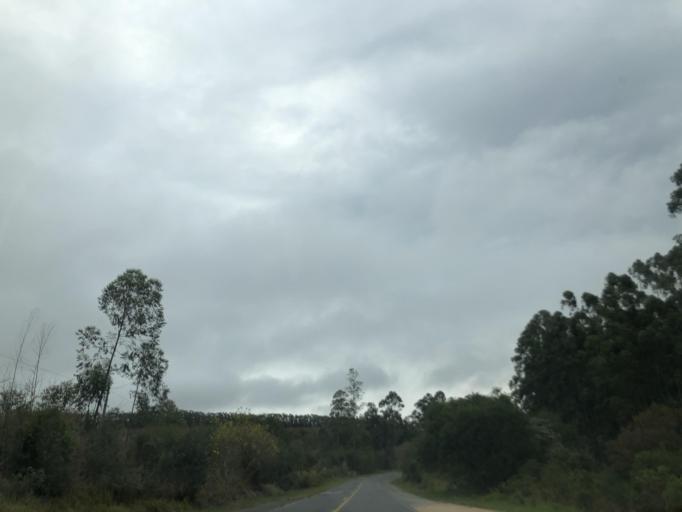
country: BR
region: Sao Paulo
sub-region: Pilar Do Sul
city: Pilar do Sul
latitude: -23.8135
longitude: -47.6460
